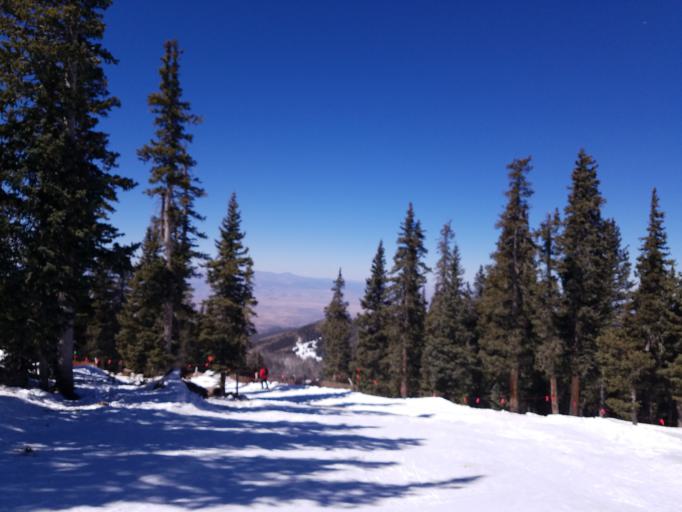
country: US
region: New Mexico
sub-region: Santa Fe County
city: Santa Fe
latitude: 35.7879
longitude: -105.7818
